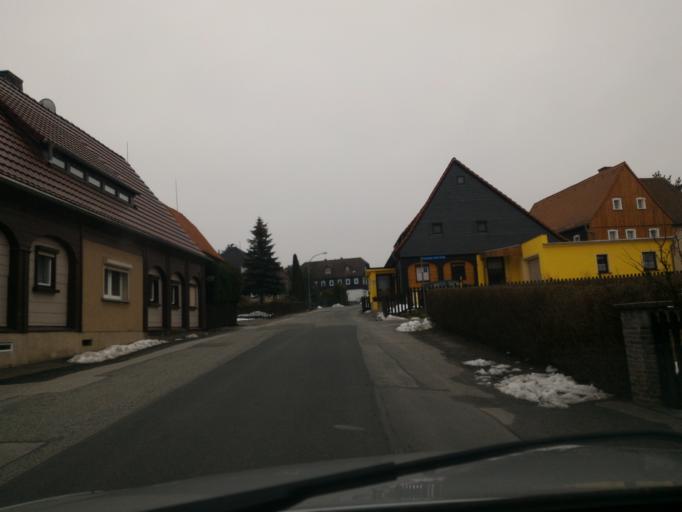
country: DE
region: Saxony
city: Neugersdorf
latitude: 50.9737
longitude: 14.6097
